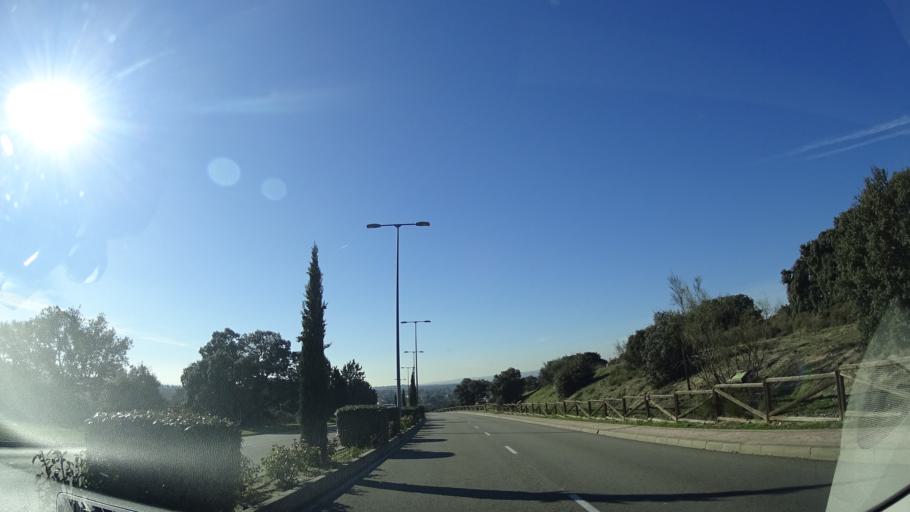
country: ES
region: Madrid
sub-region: Provincia de Madrid
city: Las Matas
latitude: 40.5300
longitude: -3.9123
